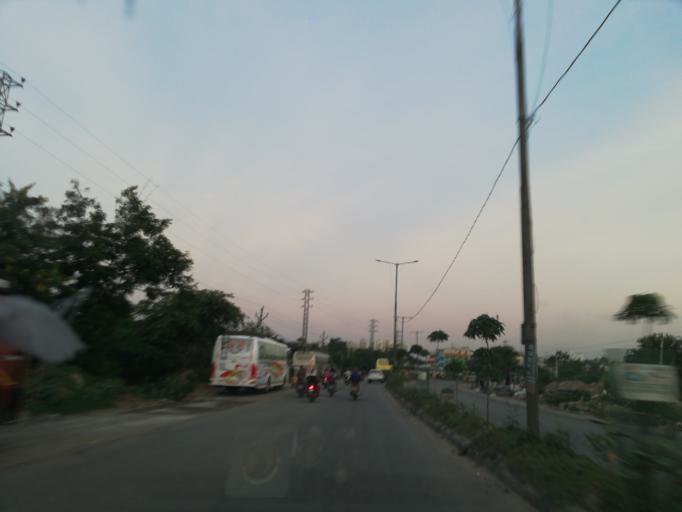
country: IN
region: Telangana
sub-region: Medak
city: Serilingampalle
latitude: 17.5158
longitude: 78.3592
